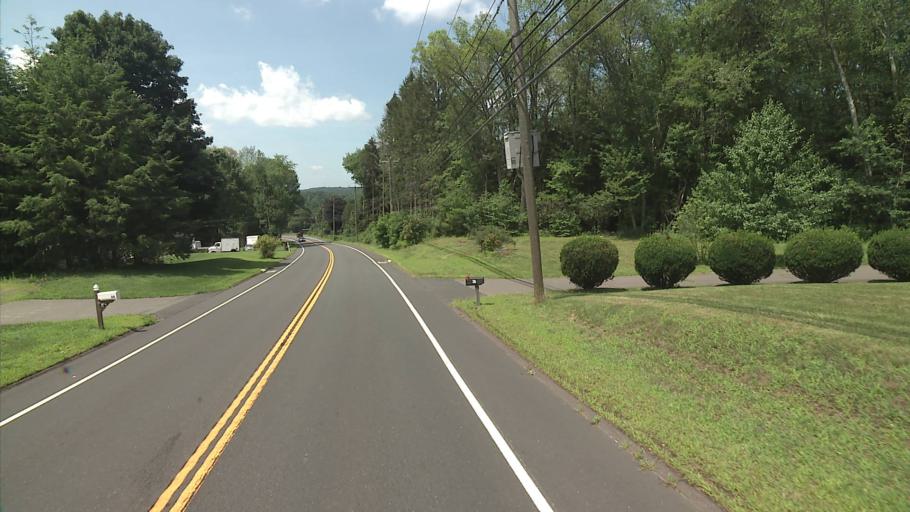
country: US
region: Connecticut
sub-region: Tolland County
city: Rockville
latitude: 41.8500
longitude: -72.4243
